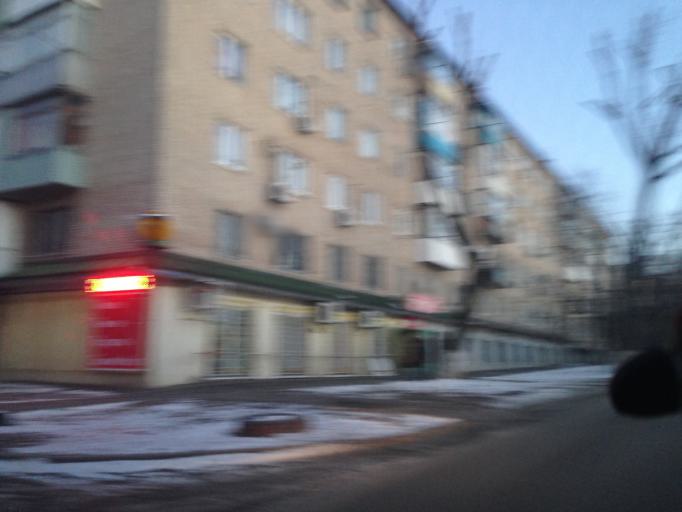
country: RU
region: Rostov
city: Severnyy
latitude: 47.2636
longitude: 39.7138
